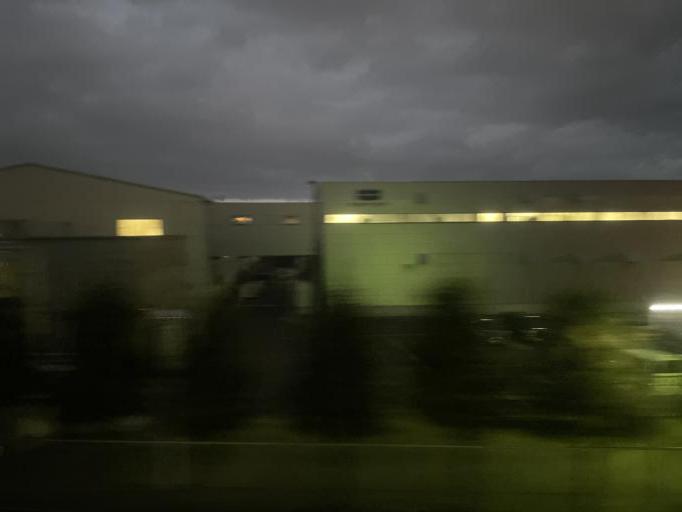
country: JP
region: Aomori
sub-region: Hachinohe Shi
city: Uchimaru
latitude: 40.5171
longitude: 141.4830
